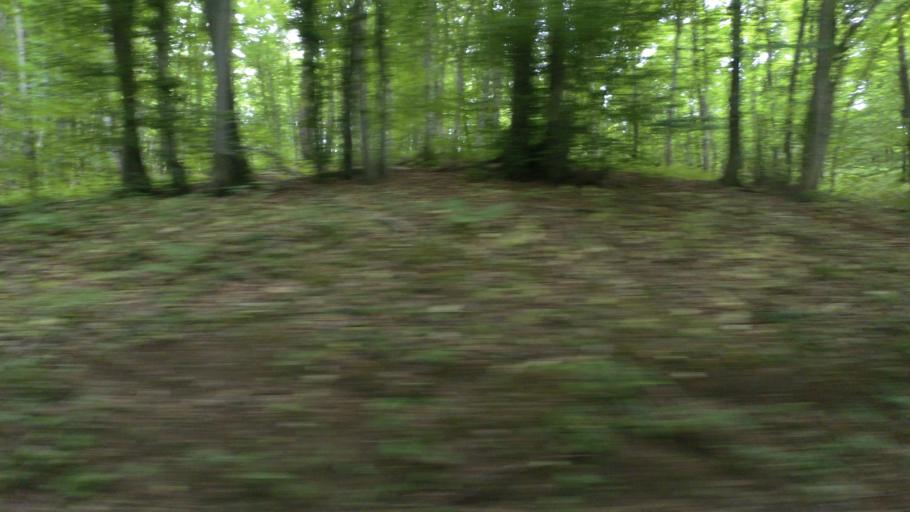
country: HR
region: Karlovacka
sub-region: Grad Karlovac
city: Karlovac
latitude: 45.4207
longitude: 15.5787
